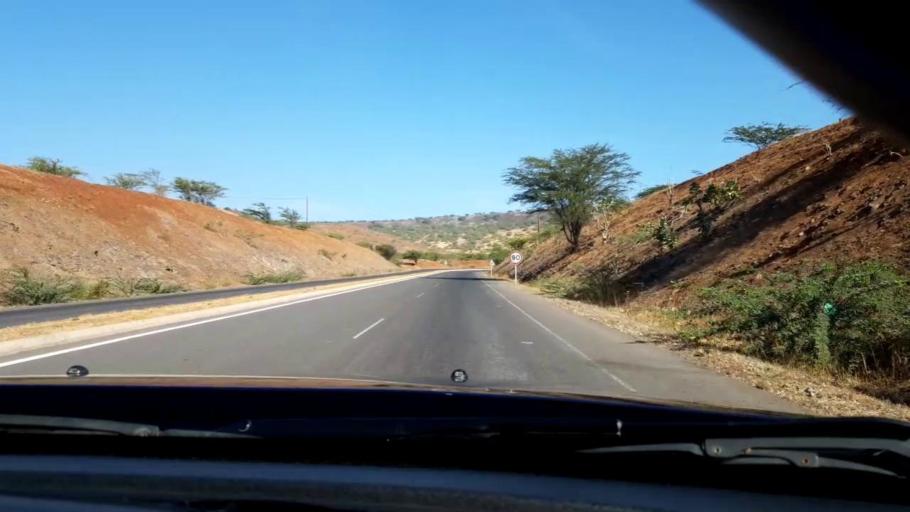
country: CV
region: Praia
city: Praia
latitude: 14.9250
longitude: -23.5505
